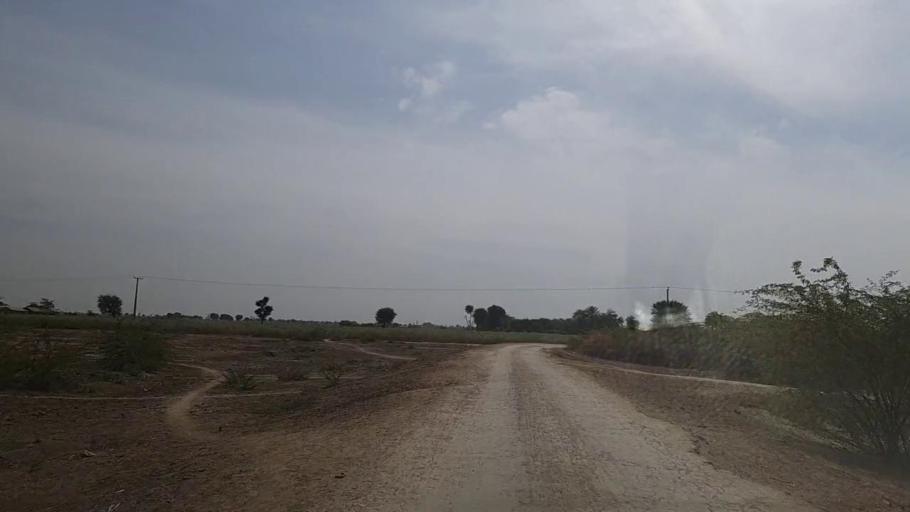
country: PK
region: Sindh
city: Samaro
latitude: 25.2123
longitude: 69.4621
